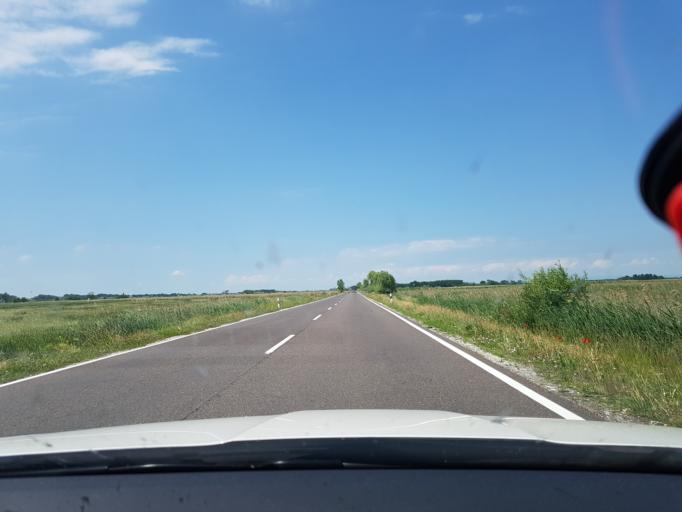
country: HU
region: Hajdu-Bihar
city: Egyek
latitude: 47.5544
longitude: 20.8742
